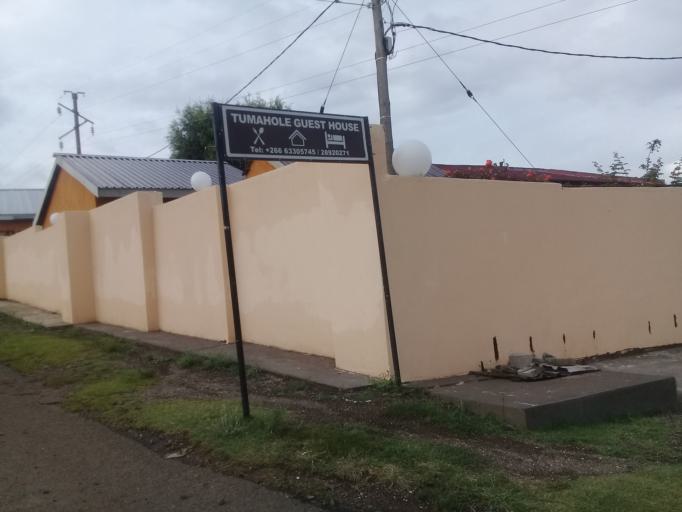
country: LS
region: Mokhotlong
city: Mokhotlong
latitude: -29.2813
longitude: 29.0658
